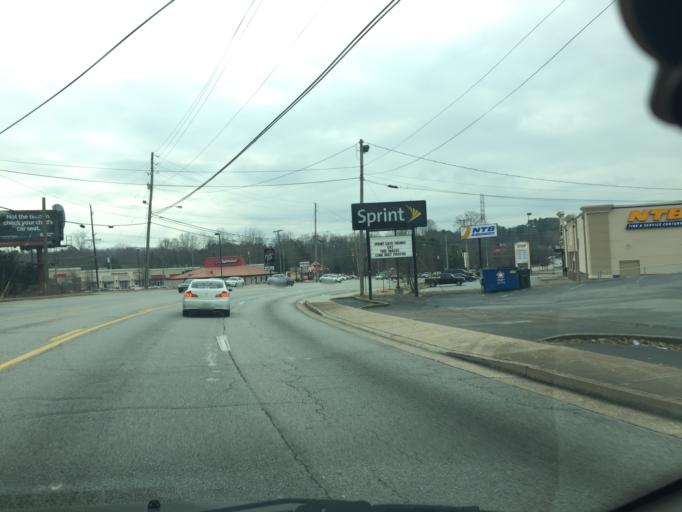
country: US
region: Tennessee
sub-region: Hamilton County
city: East Brainerd
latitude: 35.0099
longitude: -85.1539
